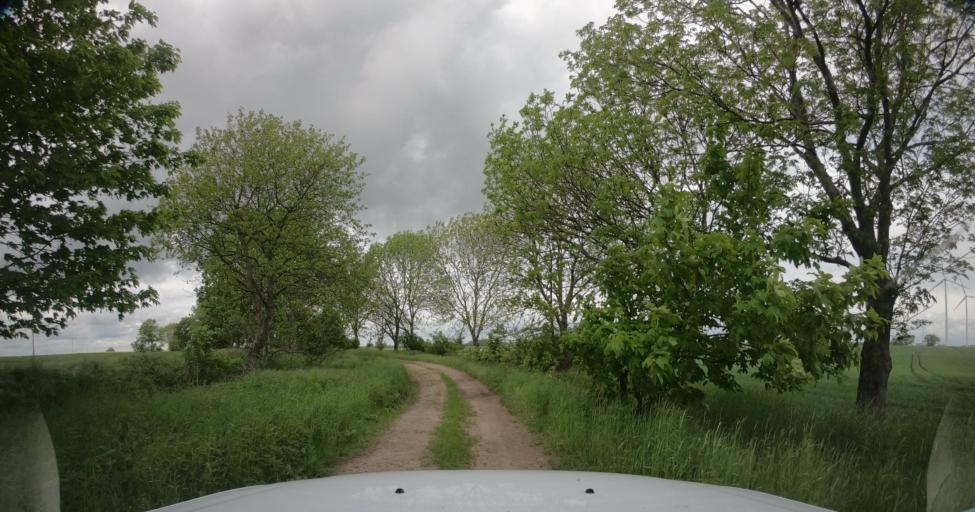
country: PL
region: West Pomeranian Voivodeship
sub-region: Powiat pyrzycki
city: Kozielice
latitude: 53.0888
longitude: 14.8233
